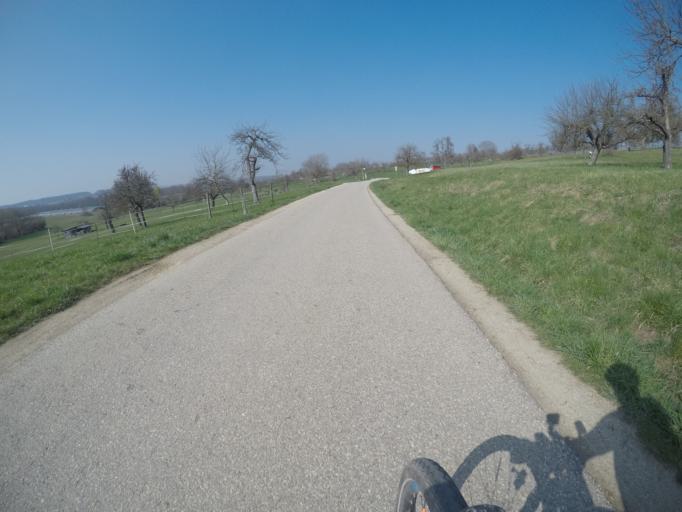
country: DE
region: Baden-Wuerttemberg
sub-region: Regierungsbezirk Stuttgart
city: Grossbettlingen
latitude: 48.6033
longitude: 9.2980
